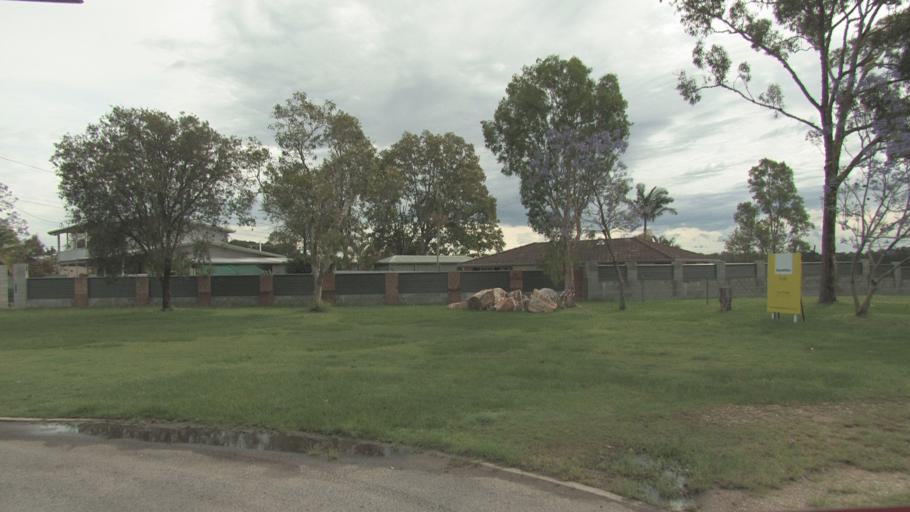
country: AU
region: Queensland
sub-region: Logan
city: Waterford West
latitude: -27.6970
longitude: 153.1234
